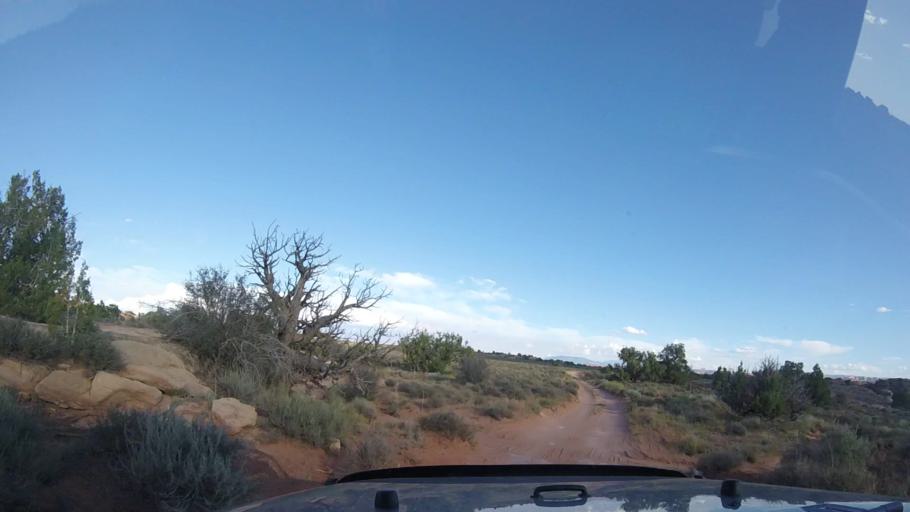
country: US
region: Utah
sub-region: Grand County
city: Moab
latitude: 38.2053
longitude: -109.7855
